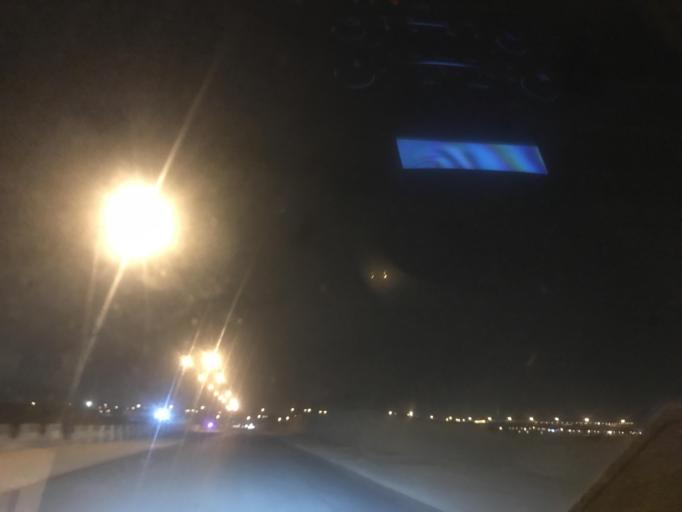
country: SA
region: Ar Riyad
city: Riyadh
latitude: 24.7616
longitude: 46.5887
